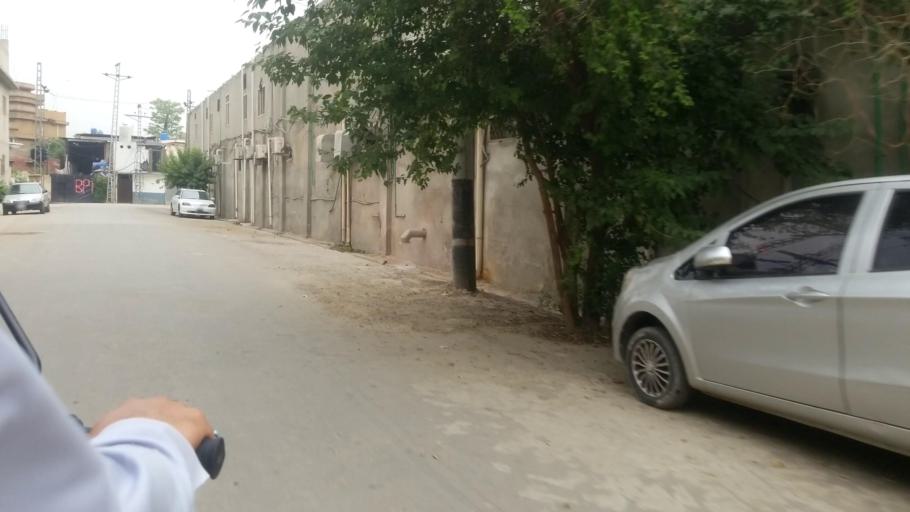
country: PK
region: Khyber Pakhtunkhwa
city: Peshawar
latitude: 33.9829
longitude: 71.5581
